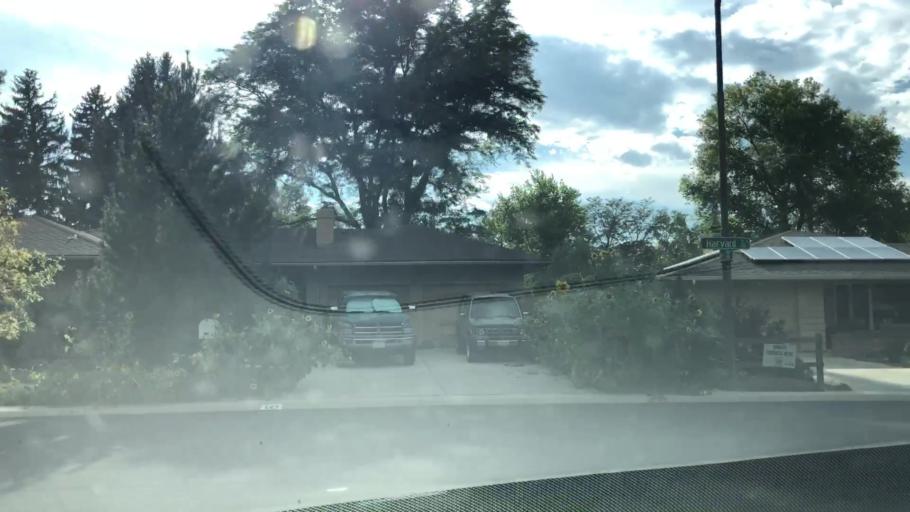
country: US
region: Colorado
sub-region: Larimer County
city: Fort Collins
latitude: 40.5541
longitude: -105.0756
